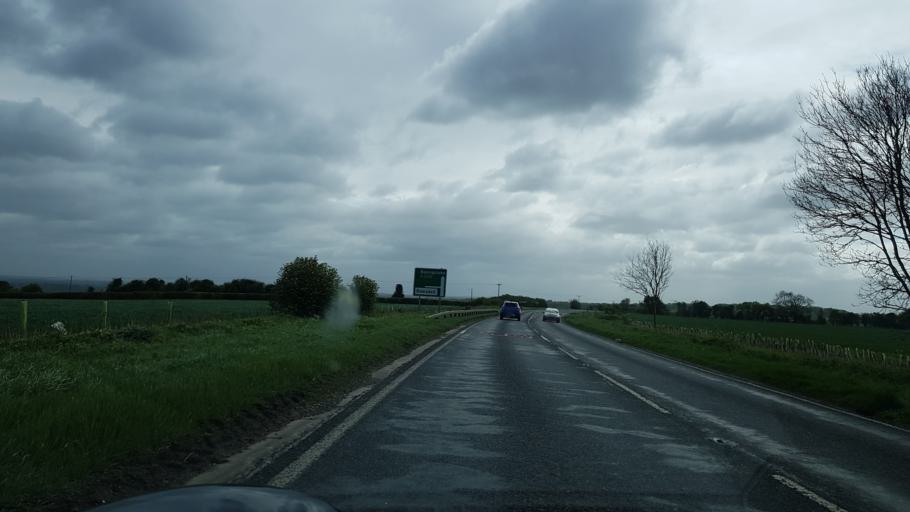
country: GB
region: England
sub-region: Hampshire
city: Tadley
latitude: 51.2892
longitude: -1.1475
